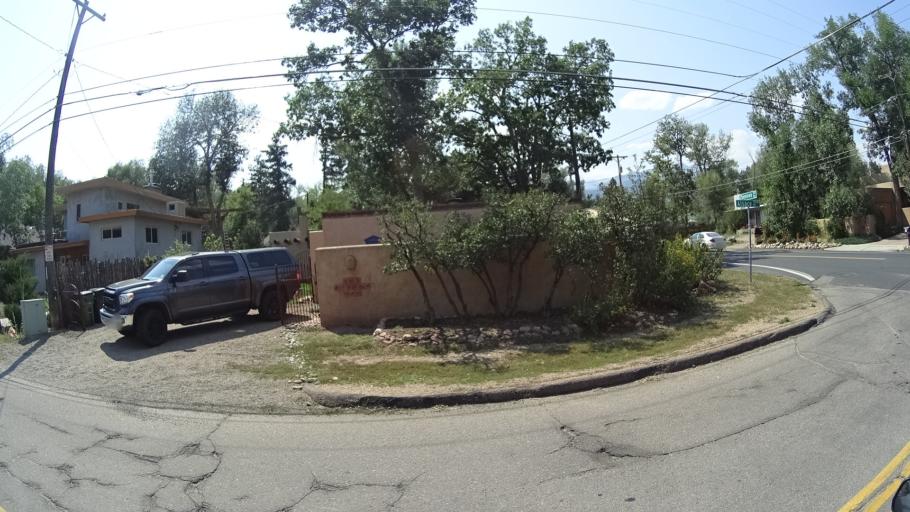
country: US
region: Colorado
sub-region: El Paso County
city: Colorado Springs
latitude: 38.8037
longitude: -104.8351
